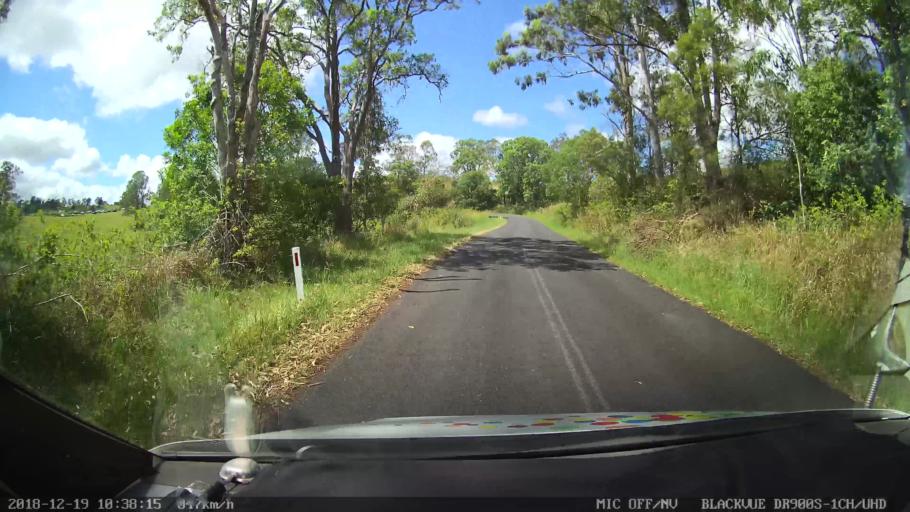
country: AU
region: New South Wales
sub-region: Lismore Municipality
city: Nimbin
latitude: -28.5740
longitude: 153.1545
